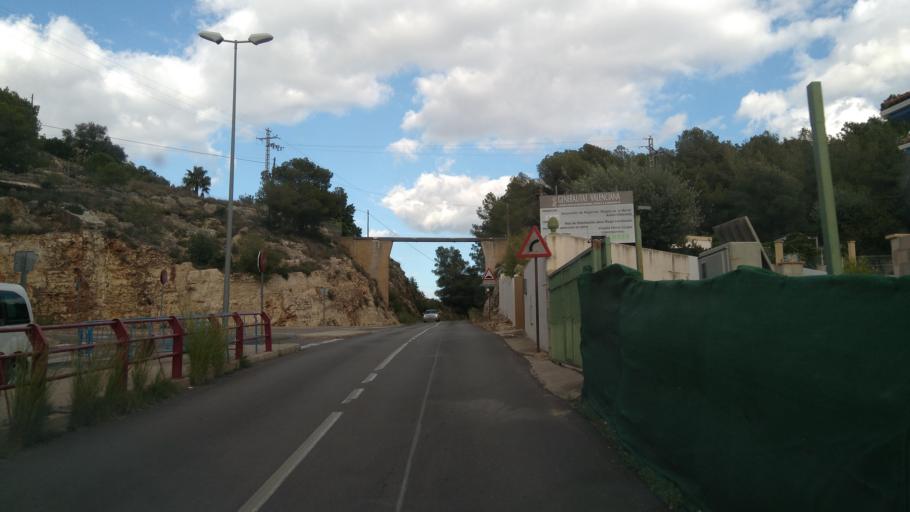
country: ES
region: Valencia
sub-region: Provincia de Valencia
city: Alzira
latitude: 39.1536
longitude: -0.4138
